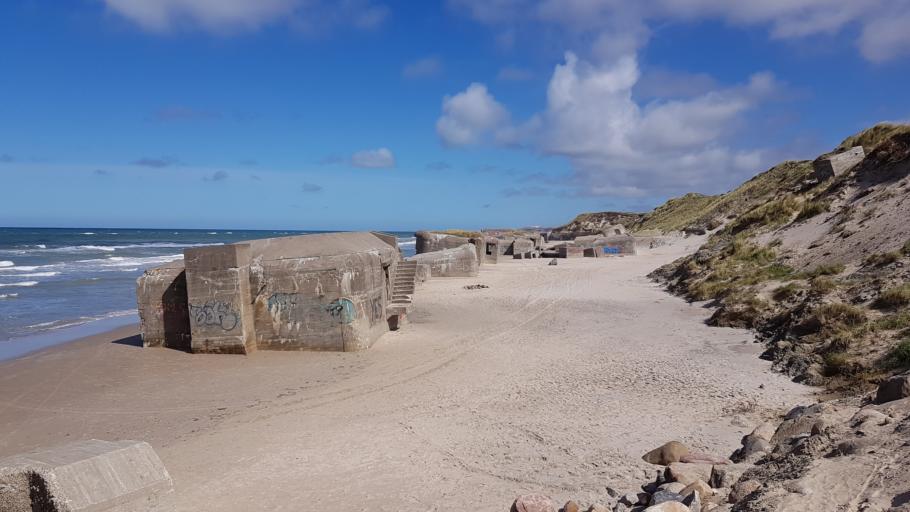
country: DK
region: North Denmark
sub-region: Jammerbugt Kommune
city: Pandrup
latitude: 57.3787
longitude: 9.7163
